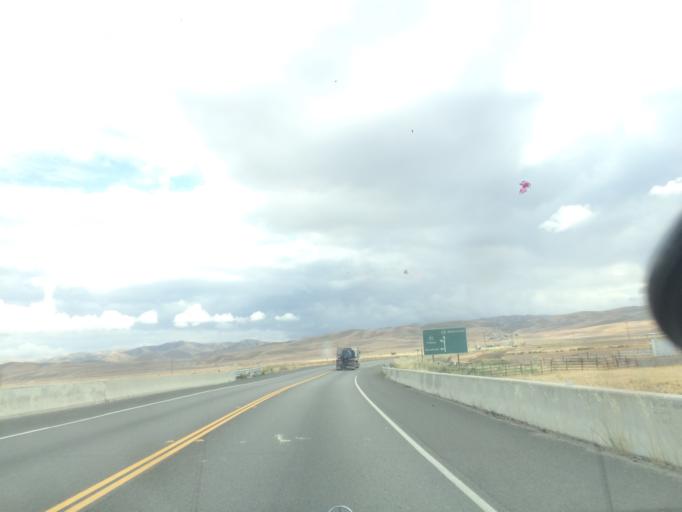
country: US
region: California
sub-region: San Luis Obispo County
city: Shandon
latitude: 35.7329
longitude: -120.2904
